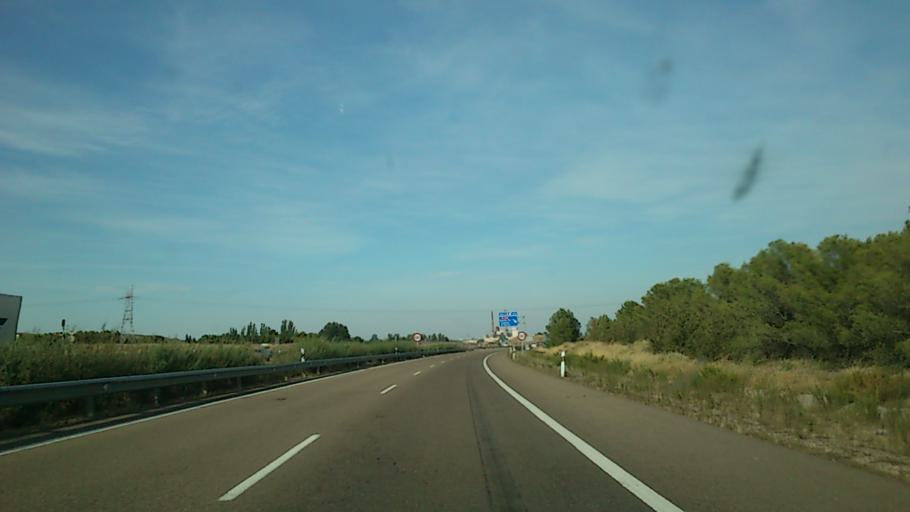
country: ES
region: Aragon
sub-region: Provincia de Zaragoza
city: Cuarte de Huerva
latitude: 41.5850
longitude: -0.9544
